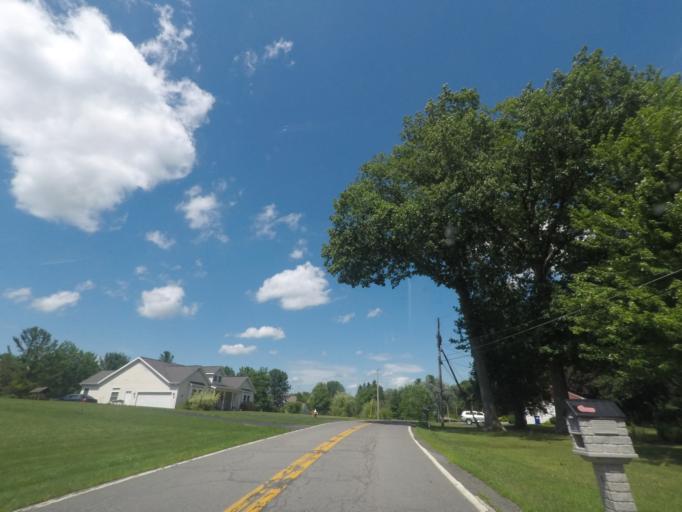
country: US
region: New York
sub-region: Schenectady County
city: Rotterdam
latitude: 42.7216
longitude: -73.9587
